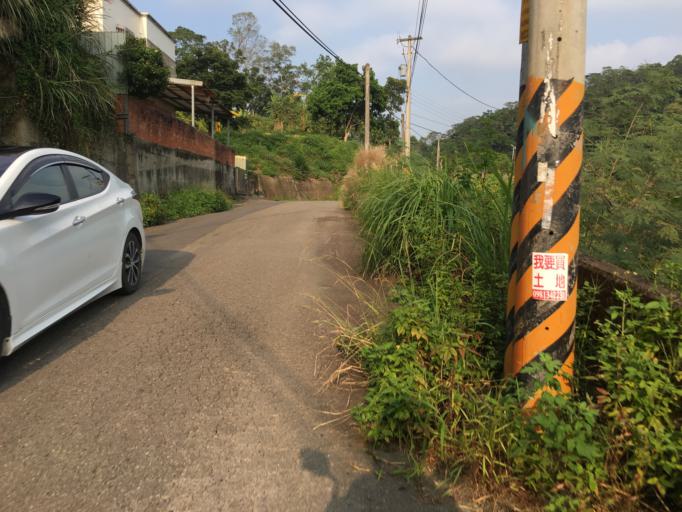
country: TW
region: Taiwan
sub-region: Hsinchu
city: Hsinchu
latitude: 24.7094
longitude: 121.0576
